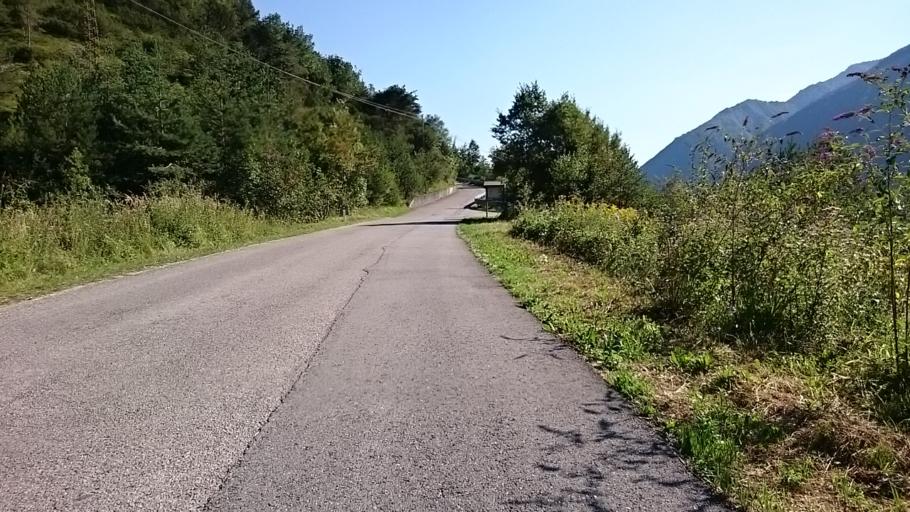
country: IT
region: Veneto
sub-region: Provincia di Belluno
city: Soverzene
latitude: 46.2176
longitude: 12.3005
